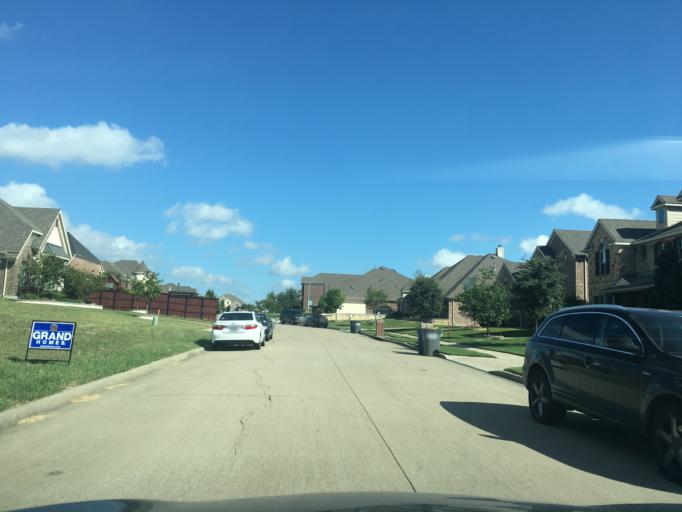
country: US
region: Texas
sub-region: Dallas County
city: Sachse
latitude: 32.9685
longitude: -96.5776
